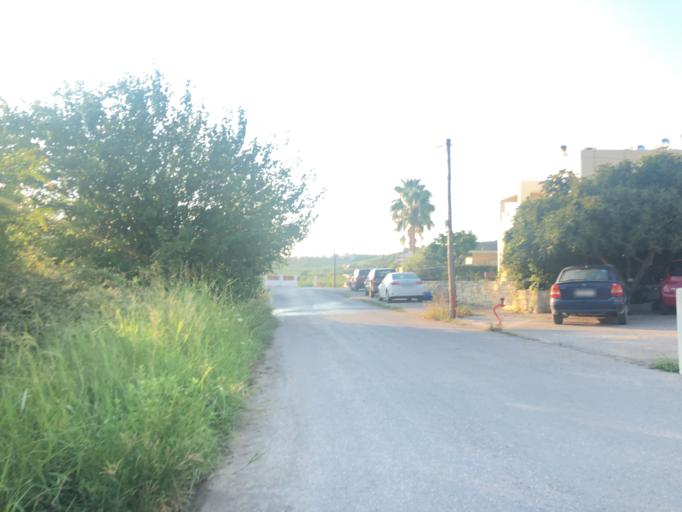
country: GR
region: Crete
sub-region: Nomos Chanias
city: Georgioupolis
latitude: 35.3456
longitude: 24.3014
